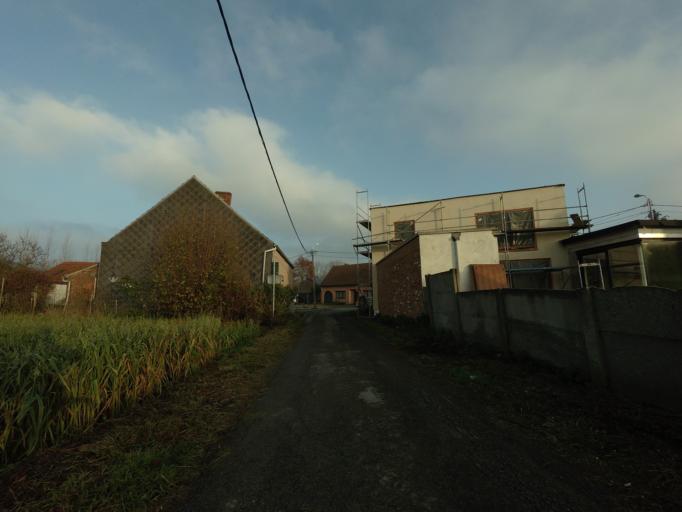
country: BE
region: Flanders
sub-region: Provincie Vlaams-Brabant
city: Herent
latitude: 50.9382
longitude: 4.6612
